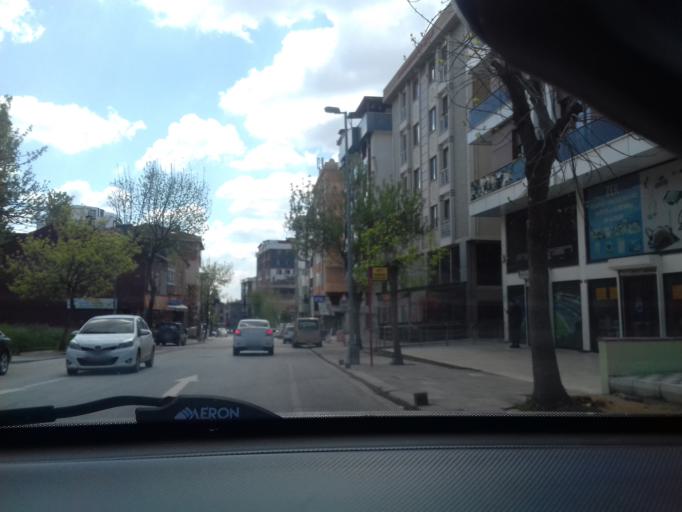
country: TR
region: Istanbul
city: Pendik
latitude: 40.8992
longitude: 29.2728
